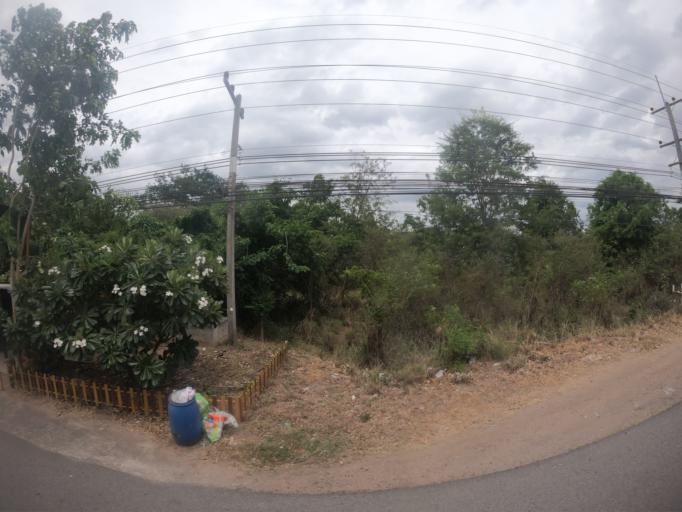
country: TH
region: Nakhon Ratchasima
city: Chok Chai
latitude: 14.8335
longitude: 102.1844
